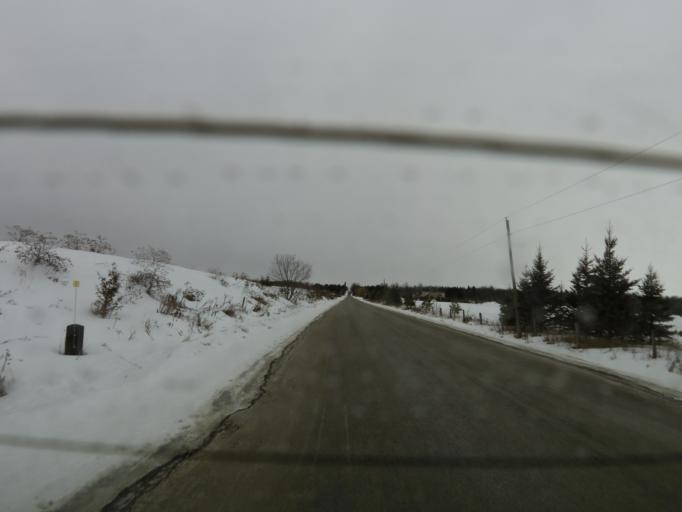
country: CA
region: Ontario
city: Clarence-Rockland
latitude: 45.4125
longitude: -75.4605
